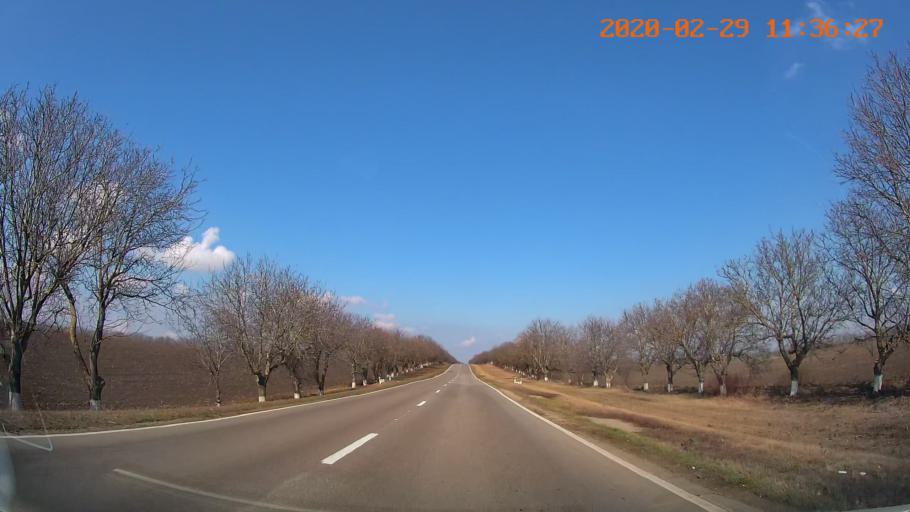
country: MD
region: Rezina
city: Saharna
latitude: 47.5962
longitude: 29.0557
